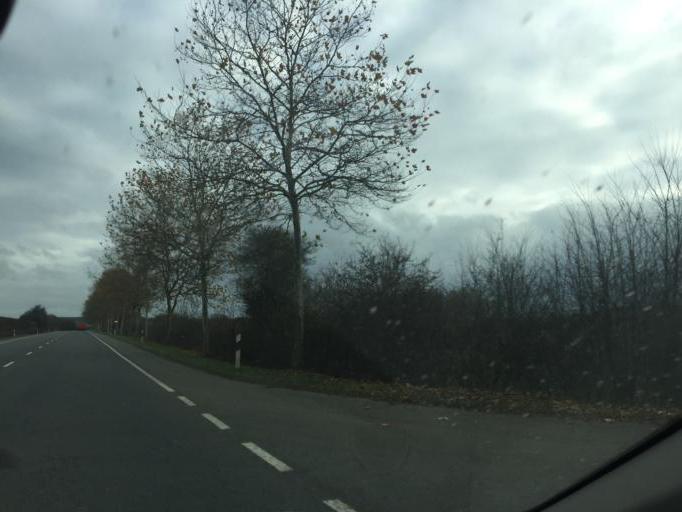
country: LU
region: Luxembourg
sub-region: Canton d'Esch-sur-Alzette
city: Frisange
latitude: 49.5179
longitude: 6.2077
